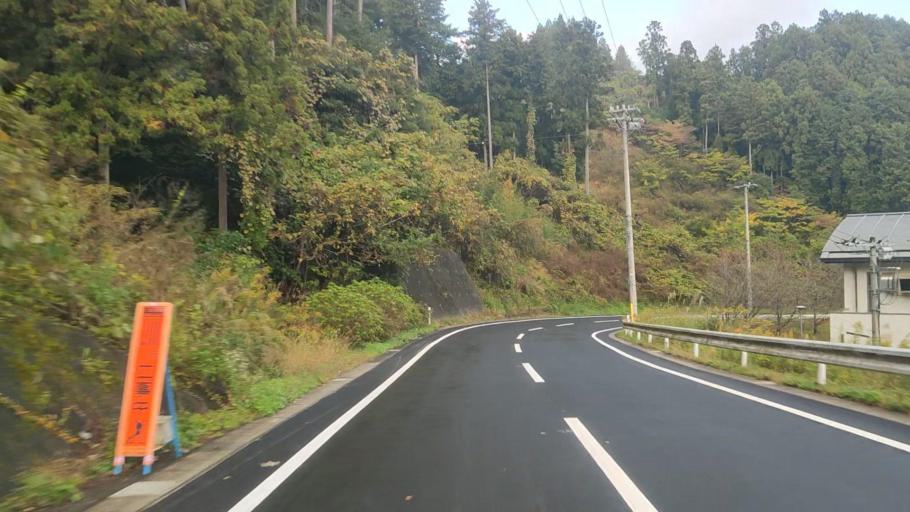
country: JP
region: Shizuoka
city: Fujinomiya
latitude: 35.2746
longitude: 138.4572
